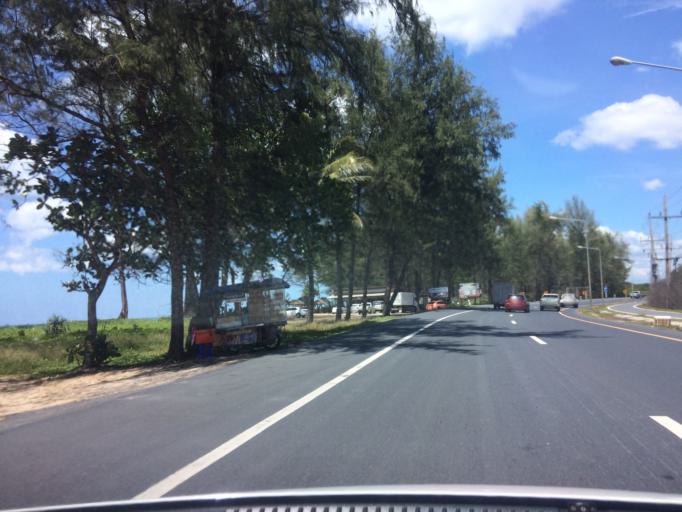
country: TH
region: Phuket
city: Thalang
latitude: 8.1887
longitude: 98.2881
